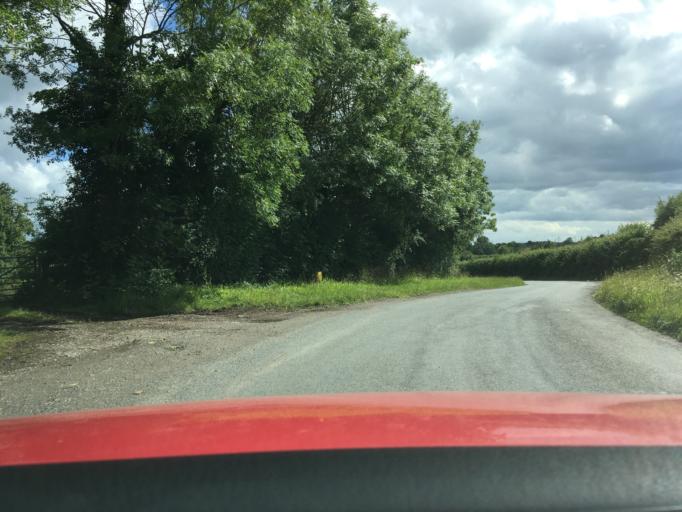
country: GB
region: England
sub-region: Gloucestershire
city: Stonehouse
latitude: 51.8313
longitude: -2.3423
